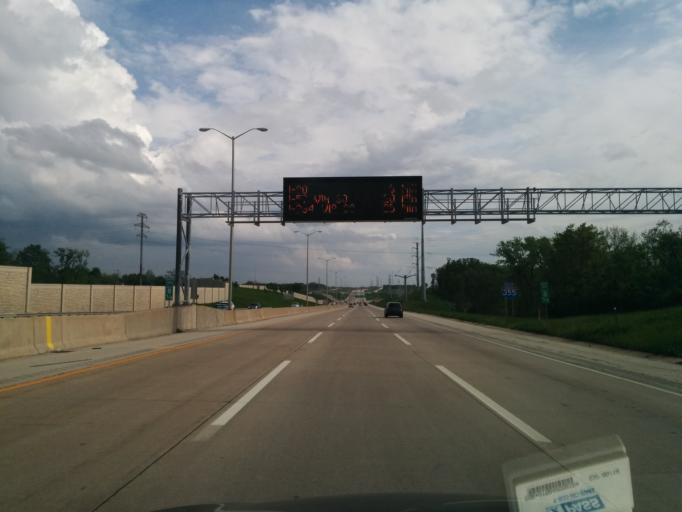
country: US
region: Illinois
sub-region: Cook County
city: Lemont
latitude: 41.6477
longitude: -88.0139
